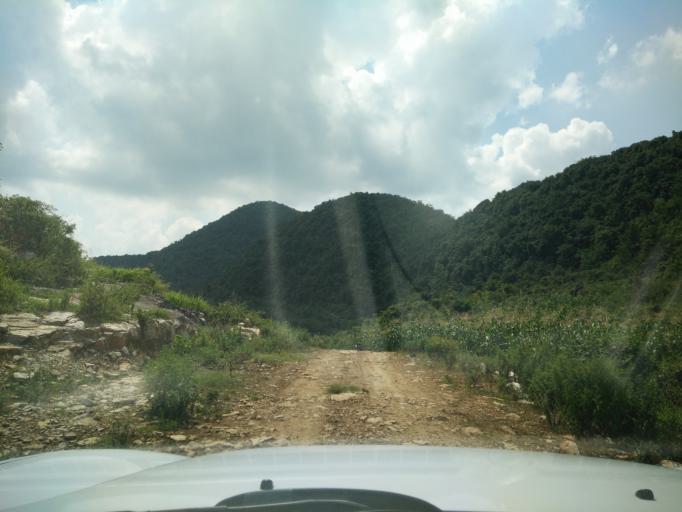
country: CN
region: Guangxi Zhuangzu Zizhiqu
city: Xinzhou
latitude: 25.1332
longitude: 105.6660
